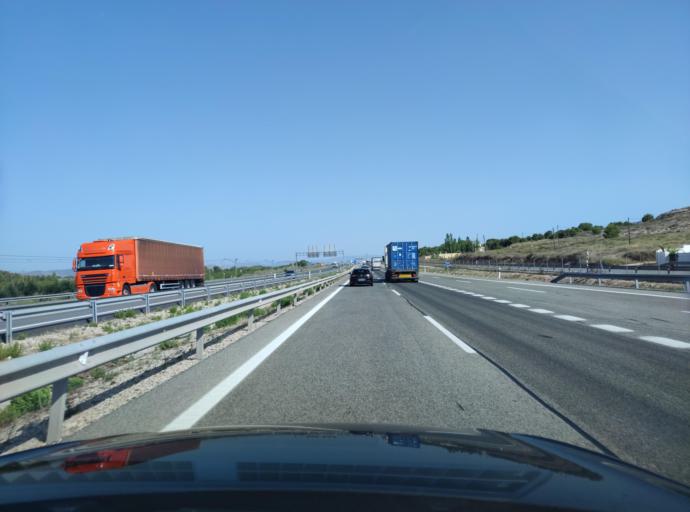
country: ES
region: Valencia
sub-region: Provincia de Alicante
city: Sax
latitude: 38.5586
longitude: -0.8277
